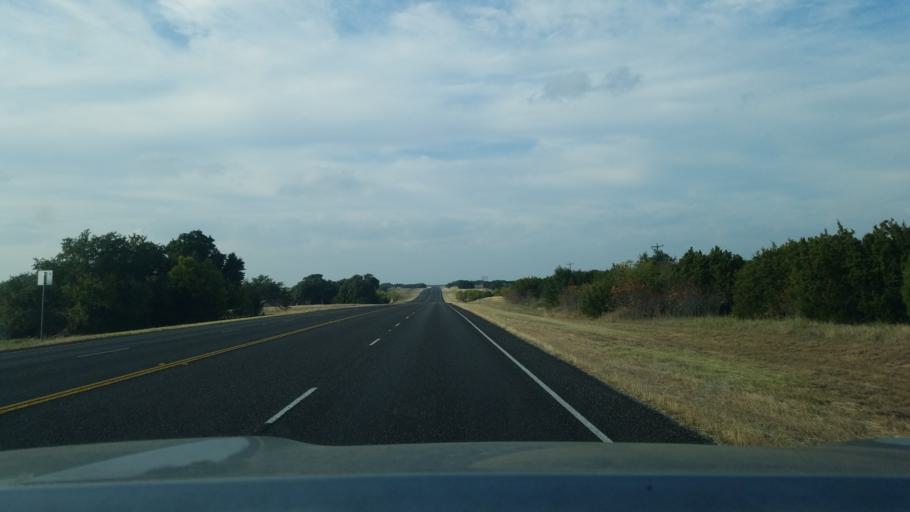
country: US
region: Texas
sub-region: Mills County
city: Goldthwaite
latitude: 31.2852
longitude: -98.4596
